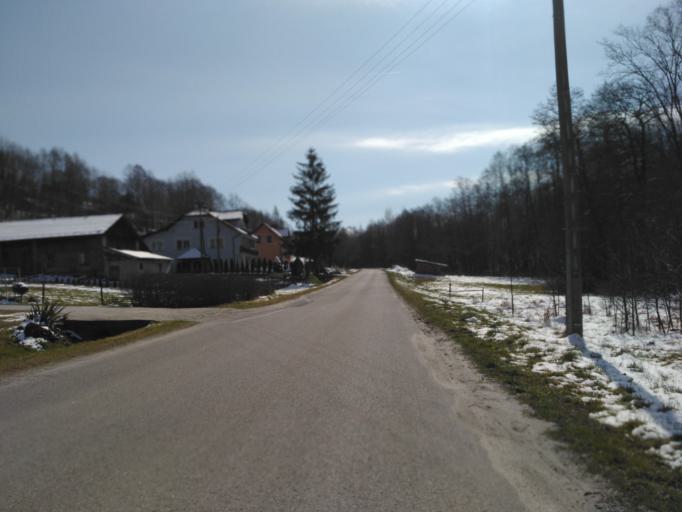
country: PL
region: Subcarpathian Voivodeship
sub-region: Powiat ropczycko-sedziszowski
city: Wielopole Skrzynskie
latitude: 49.9885
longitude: 21.5859
